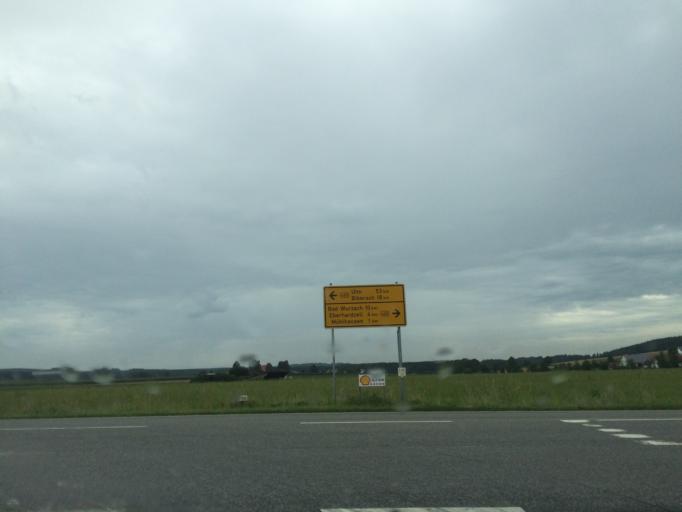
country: DE
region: Baden-Wuerttemberg
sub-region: Tuebingen Region
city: Eberhardzell
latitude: 47.9650
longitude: 9.8111
